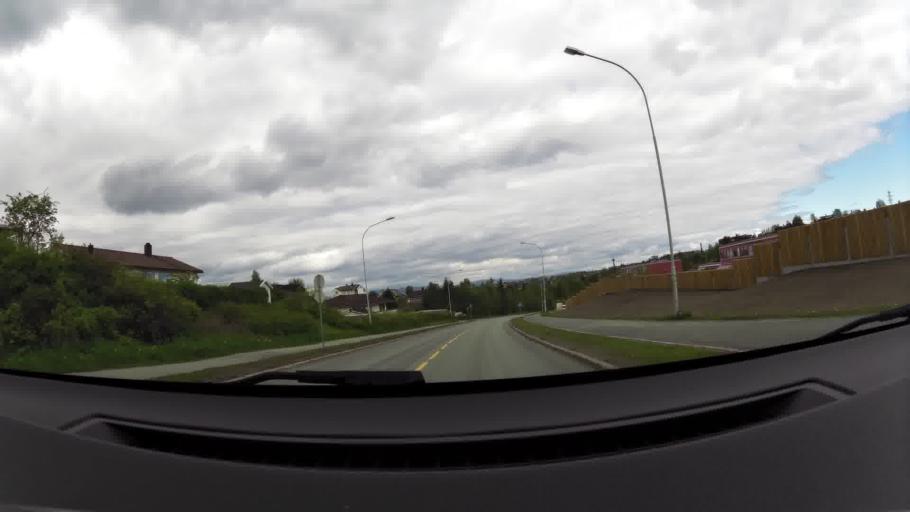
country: NO
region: Sor-Trondelag
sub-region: Trondheim
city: Trondheim
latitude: 63.3964
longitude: 10.4222
